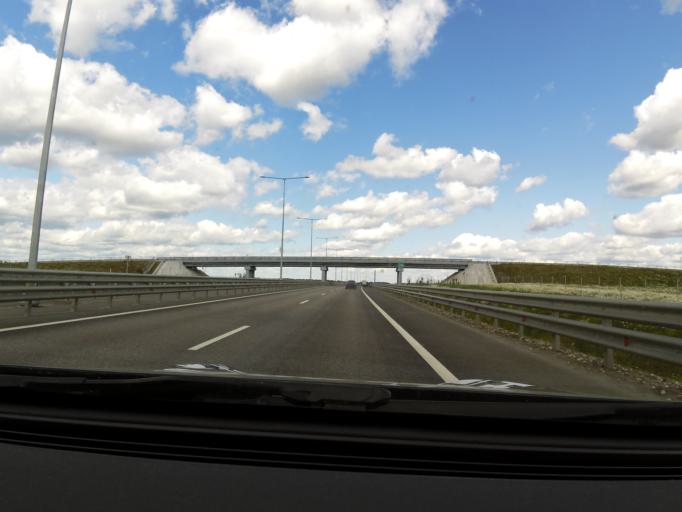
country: RU
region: Tverskaya
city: Vydropuzhsk
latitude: 57.2427
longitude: 34.8944
